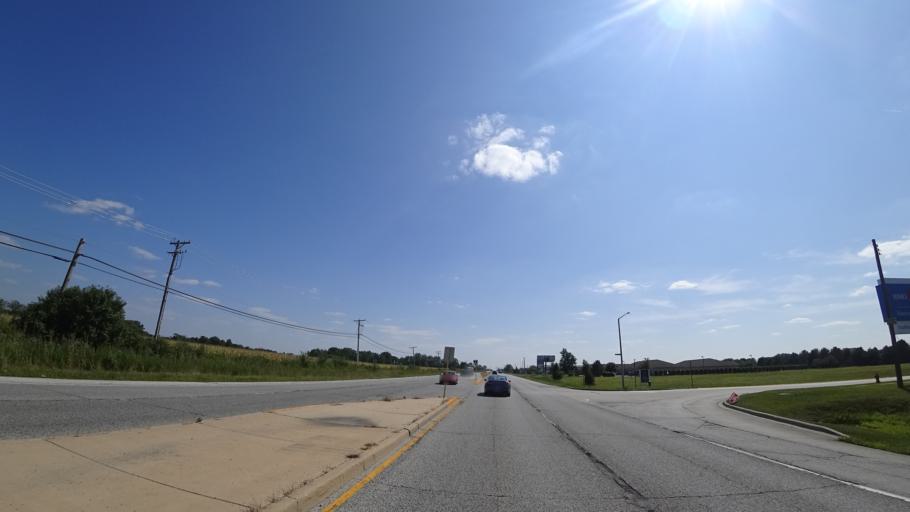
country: US
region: Illinois
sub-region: Will County
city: Frankfort Square
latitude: 41.5358
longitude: -87.7904
